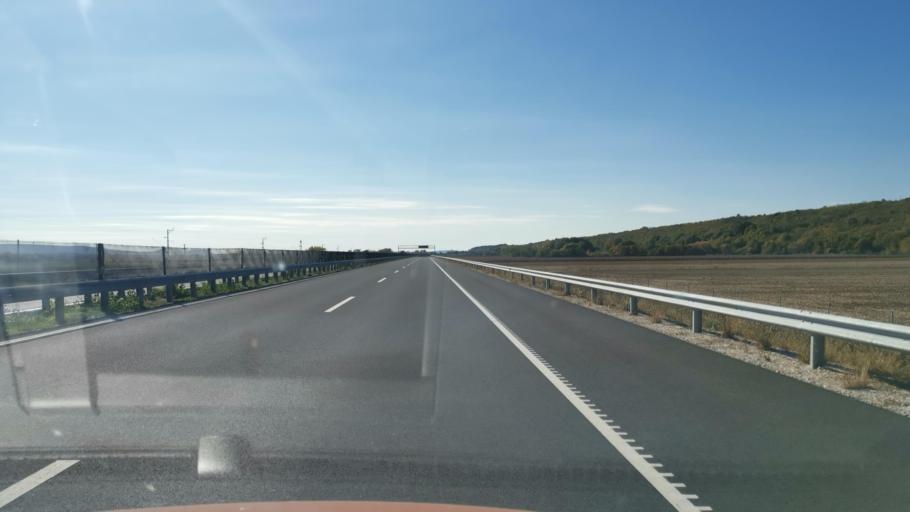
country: HU
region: Borsod-Abauj-Zemplen
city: Gonc
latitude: 48.4430
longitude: 21.1906
